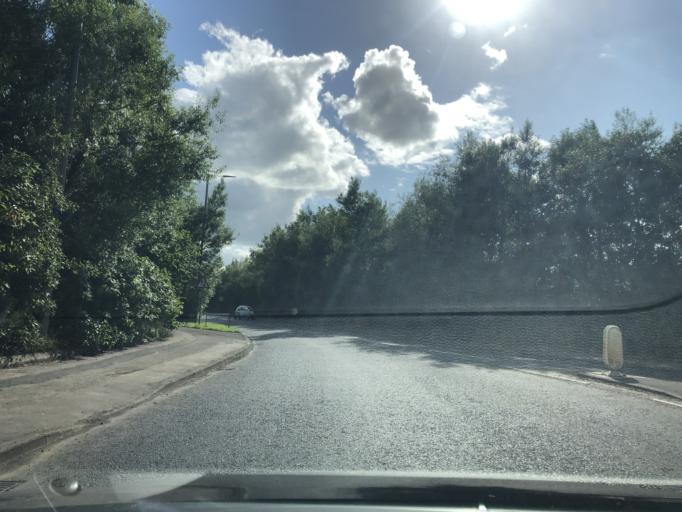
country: GB
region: Northern Ireland
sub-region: Ards District
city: Comber
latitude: 54.5510
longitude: -5.7298
